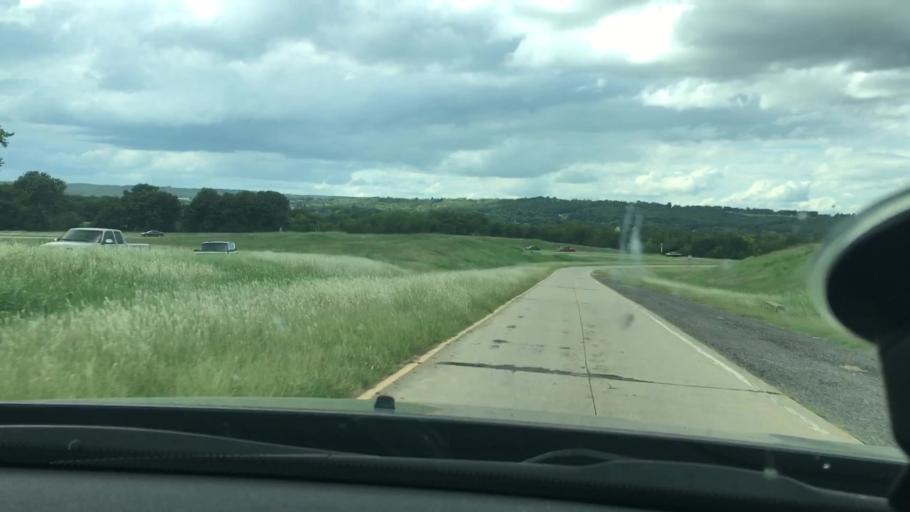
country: US
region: Oklahoma
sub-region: Okmulgee County
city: Henryetta
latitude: 35.4331
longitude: -95.9689
